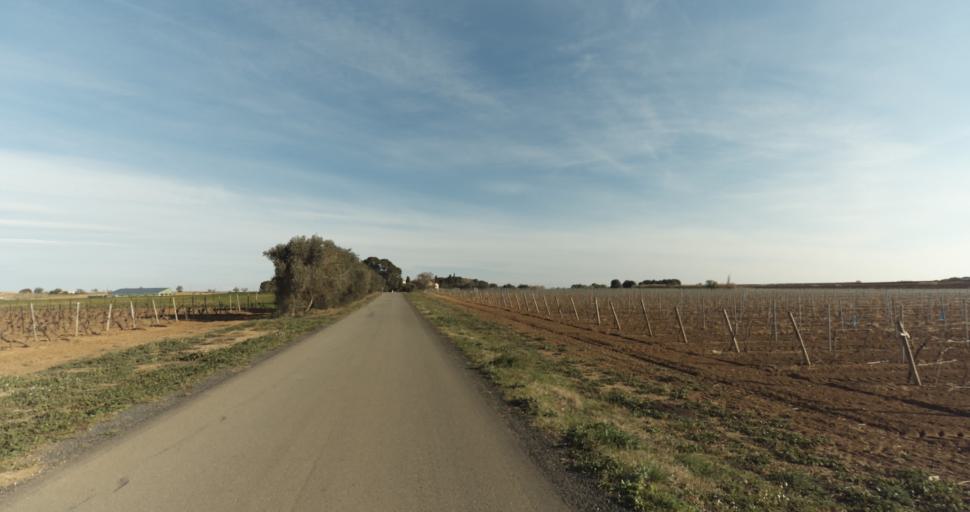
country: FR
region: Languedoc-Roussillon
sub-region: Departement de l'Herault
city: Pomerols
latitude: 43.3791
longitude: 3.5185
